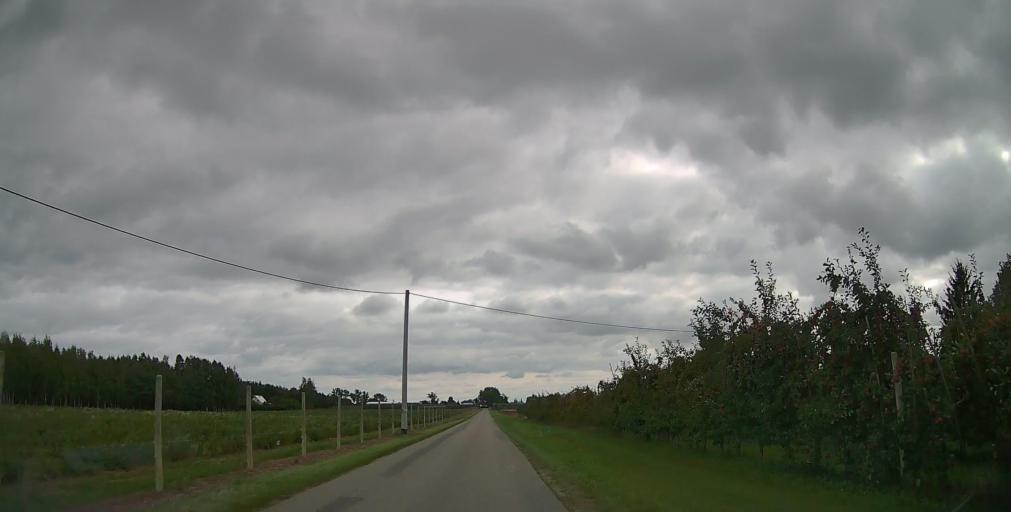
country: PL
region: Masovian Voivodeship
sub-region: Powiat grojecki
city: Goszczyn
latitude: 51.7645
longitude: 20.8692
